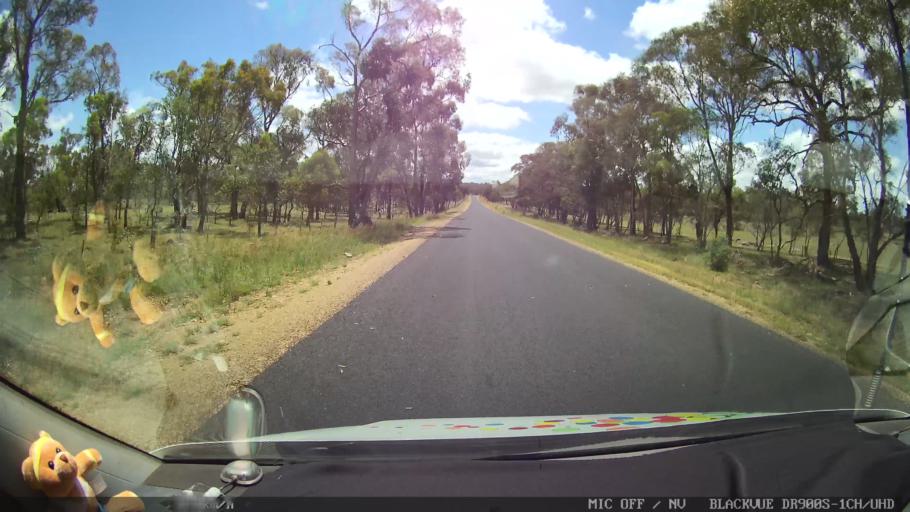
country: AU
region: New South Wales
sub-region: Glen Innes Severn
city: Glen Innes
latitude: -29.4303
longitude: 151.6939
